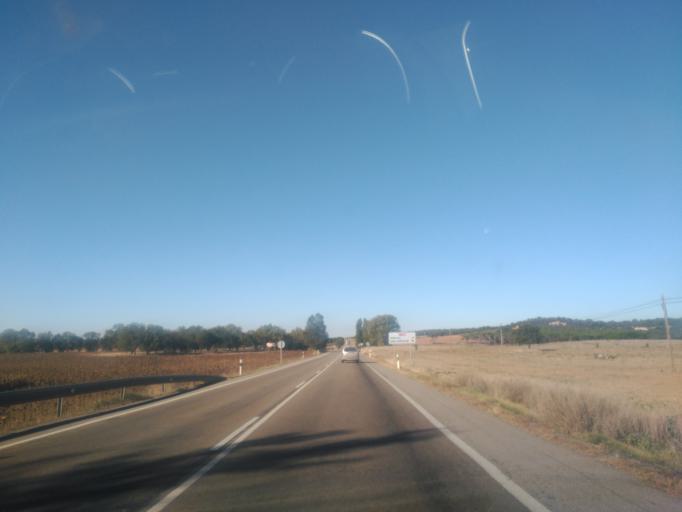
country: ES
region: Castille and Leon
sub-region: Provincia de Burgos
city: Valdezate
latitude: 41.6142
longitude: -3.9326
